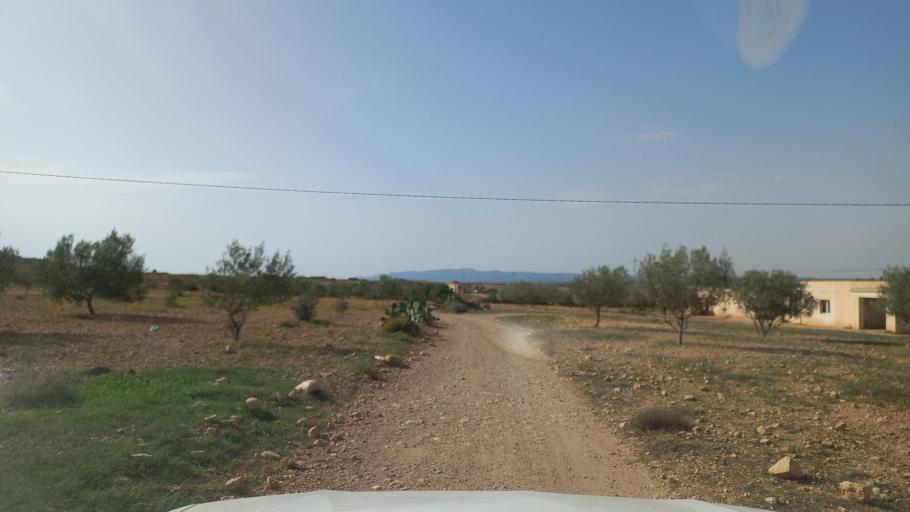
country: TN
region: Al Qasrayn
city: Kasserine
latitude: 35.3383
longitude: 8.8216
